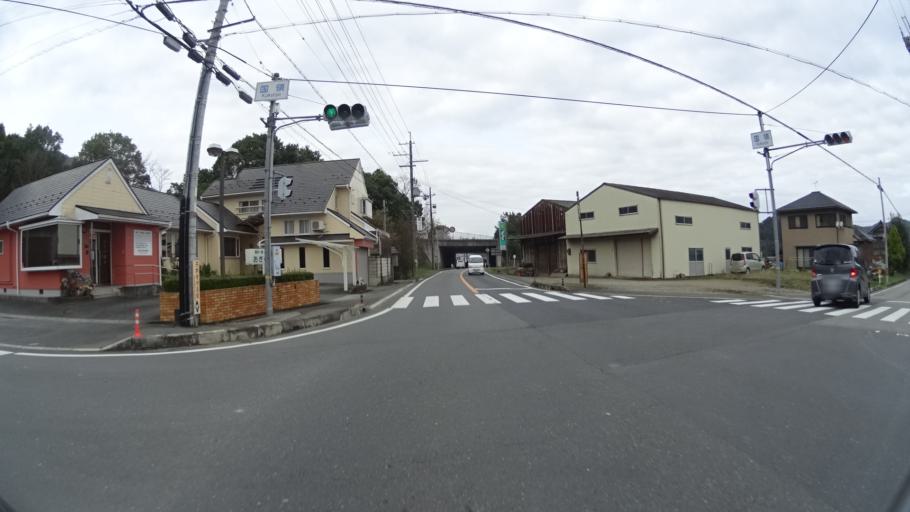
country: JP
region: Hyogo
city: Sasayama
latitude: 35.1446
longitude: 135.1274
